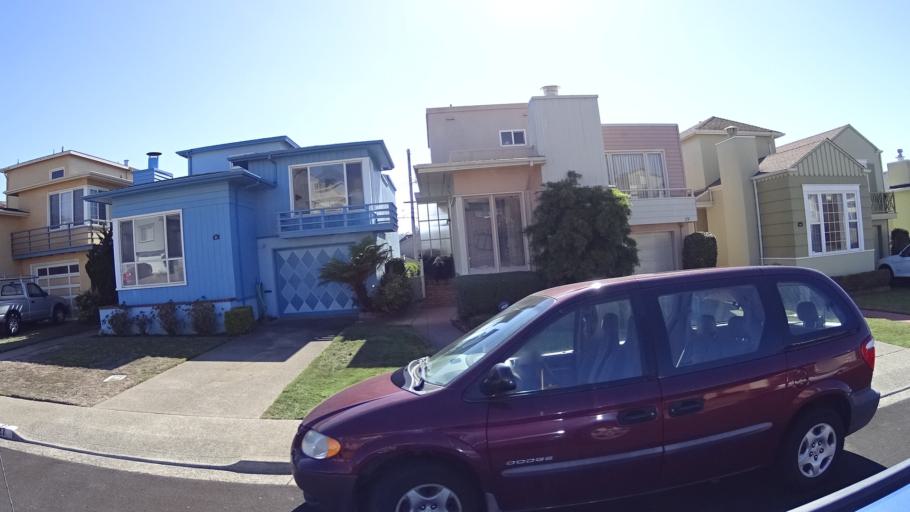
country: US
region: California
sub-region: San Mateo County
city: Daly City
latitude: 37.7060
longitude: -122.4774
